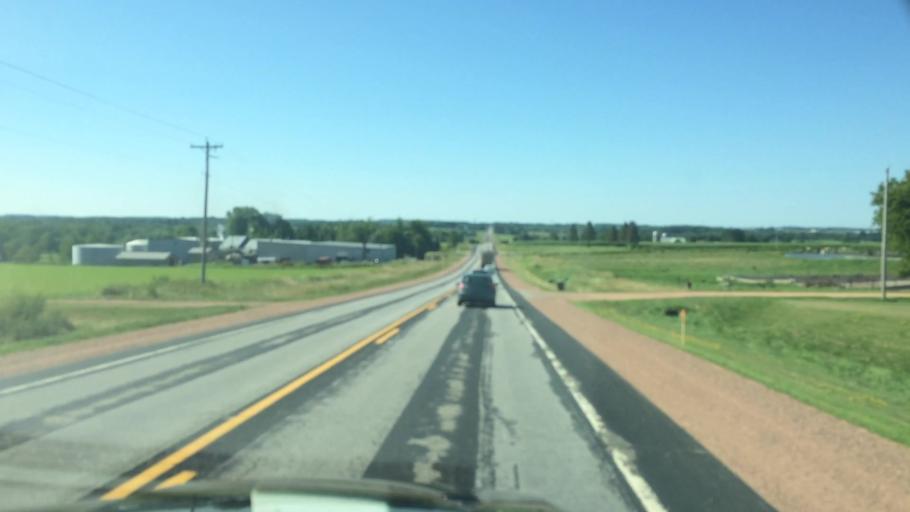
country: US
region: Wisconsin
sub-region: Marathon County
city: Stratford
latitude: 44.8331
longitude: -90.0792
